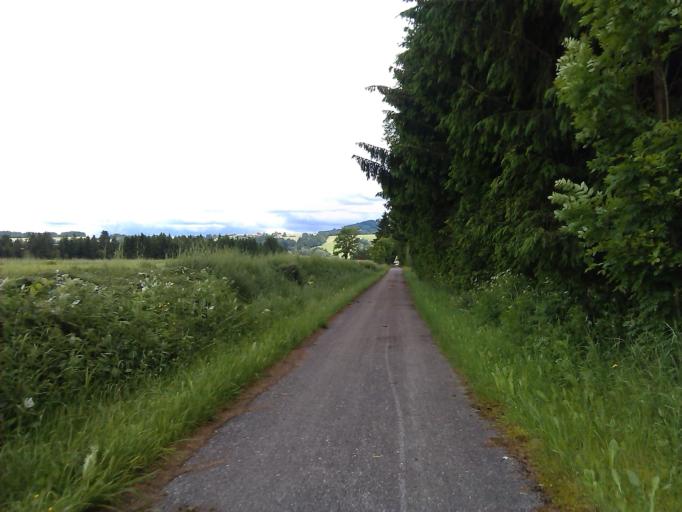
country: DE
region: Bavaria
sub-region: Swabia
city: Stotten am Auerberg
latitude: 47.7478
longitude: 10.6681
